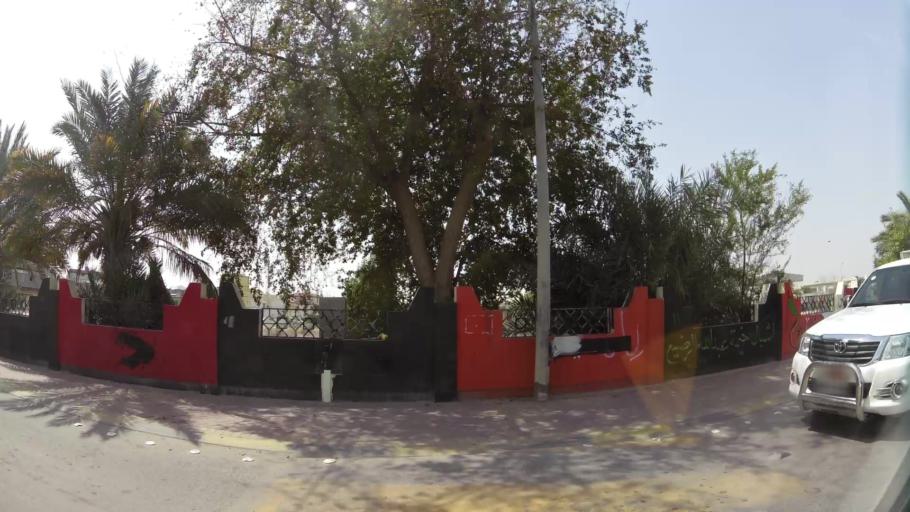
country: BH
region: Manama
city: Jidd Hafs
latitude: 26.2296
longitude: 50.4794
